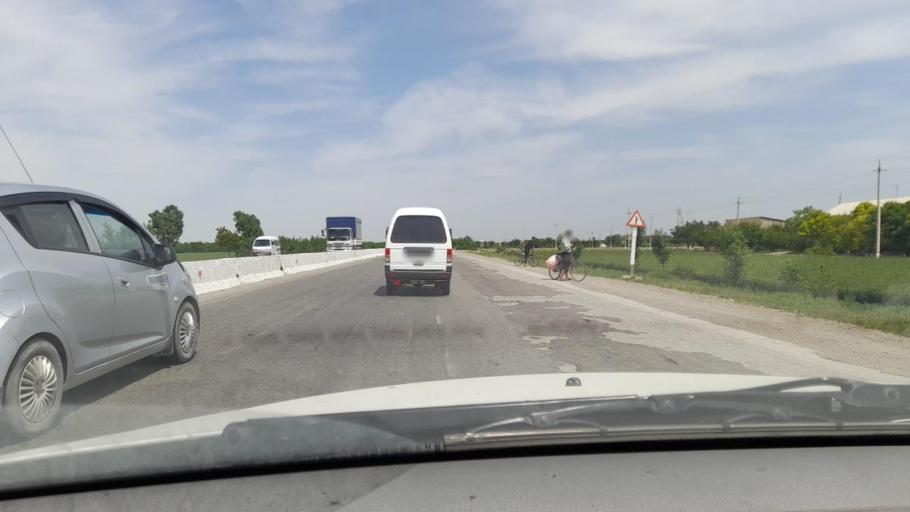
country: UZ
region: Bukhara
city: Wobkent
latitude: 40.0455
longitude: 64.5381
